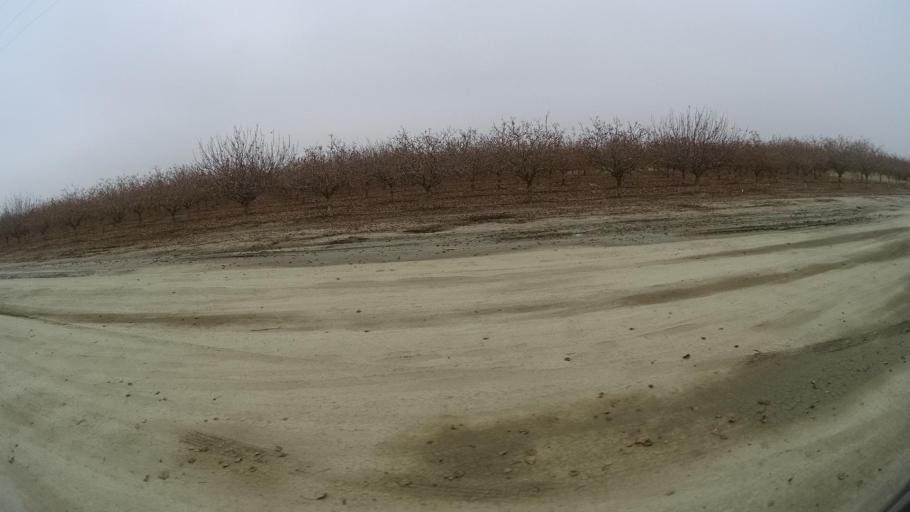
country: US
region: California
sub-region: Kern County
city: Wasco
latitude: 35.6859
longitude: -119.4909
